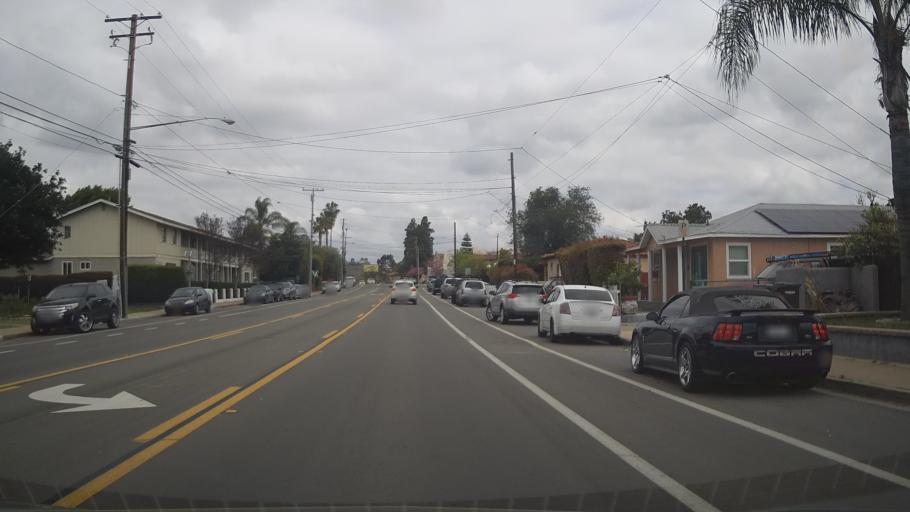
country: US
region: California
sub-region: San Diego County
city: La Mesa
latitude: 32.7646
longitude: -117.0469
